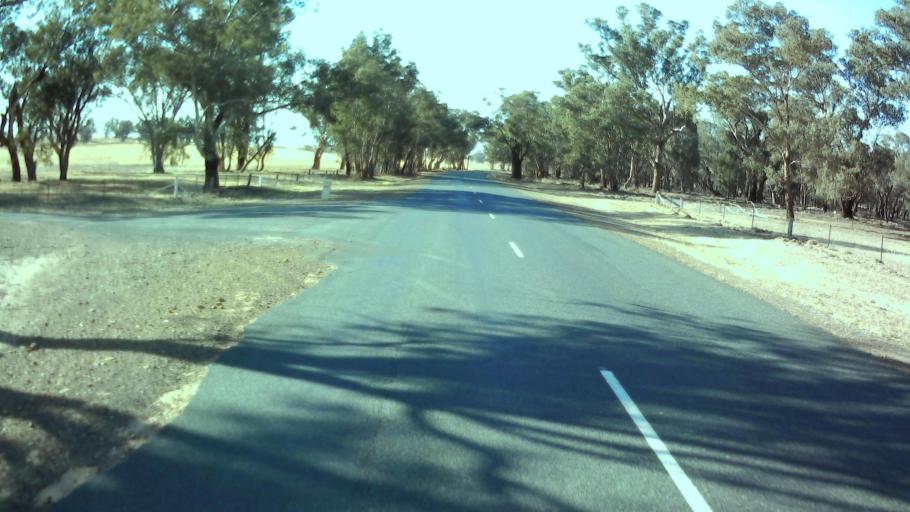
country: AU
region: New South Wales
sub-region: Weddin
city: Grenfell
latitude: -33.9494
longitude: 148.1377
